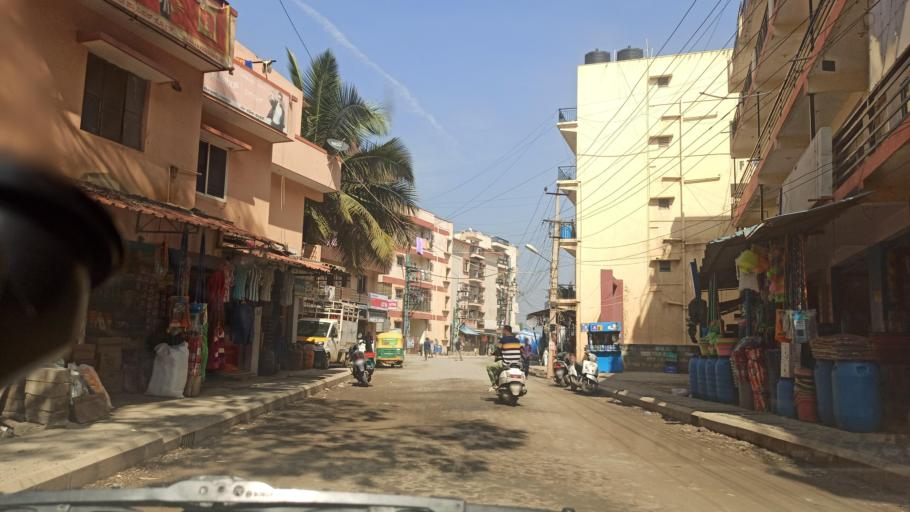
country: IN
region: Karnataka
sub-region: Bangalore Urban
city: Bangalore
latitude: 12.9267
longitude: 77.6896
